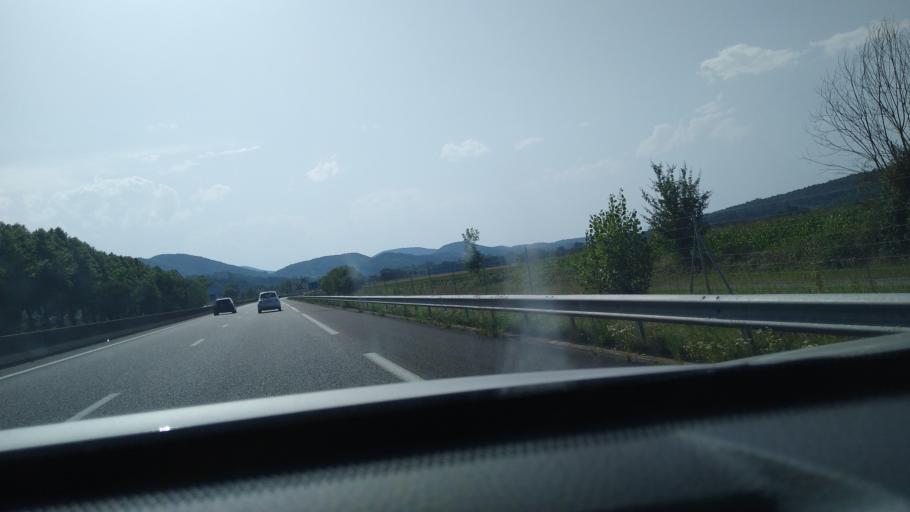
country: FR
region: Midi-Pyrenees
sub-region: Departement de la Haute-Garonne
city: Salies-du-Salat
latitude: 43.0335
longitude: 1.0360
